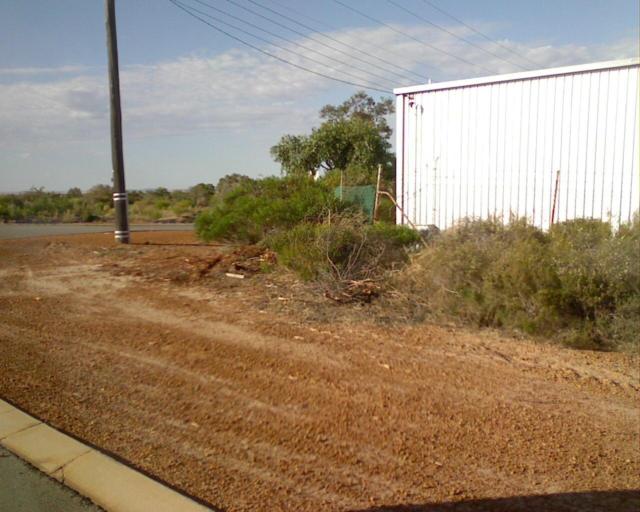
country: AU
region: Western Australia
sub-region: Dandaragan
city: Jurien Bay
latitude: -29.8173
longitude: 115.2762
